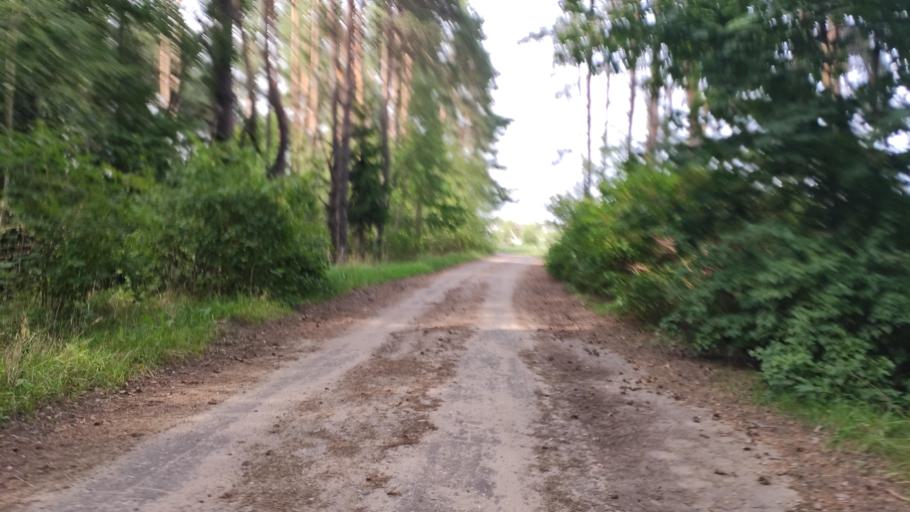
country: BY
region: Minsk
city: Narach
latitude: 54.9295
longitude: 26.6787
